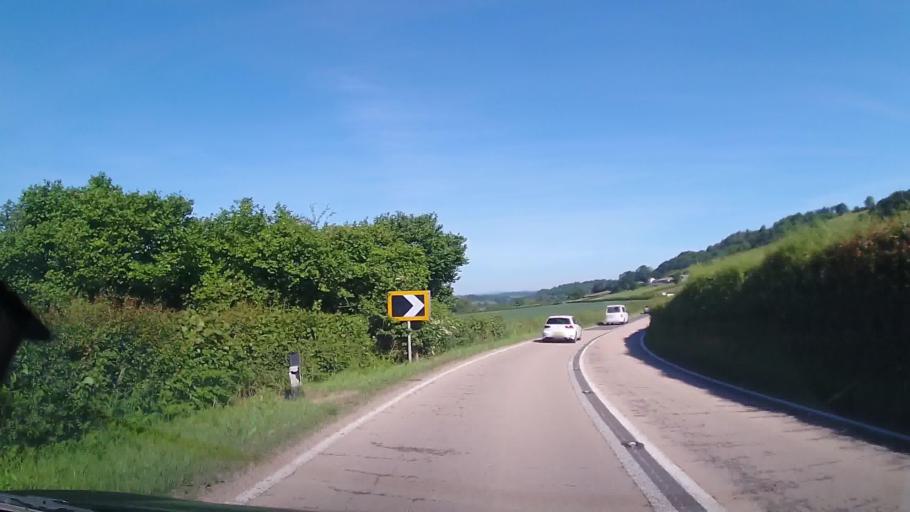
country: GB
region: Wales
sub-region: Sir Powys
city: Welshpool
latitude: 52.6504
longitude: -3.2504
